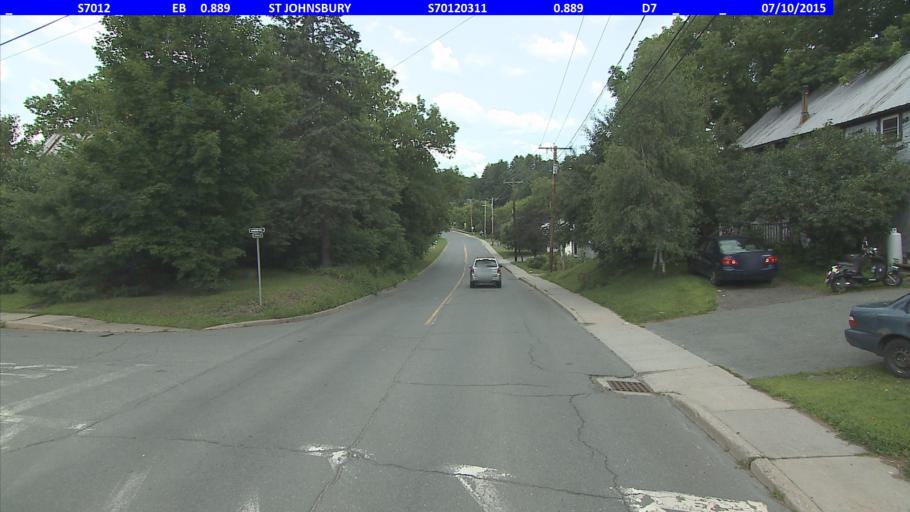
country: US
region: Vermont
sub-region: Caledonia County
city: St Johnsbury
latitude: 44.4224
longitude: -72.0068
